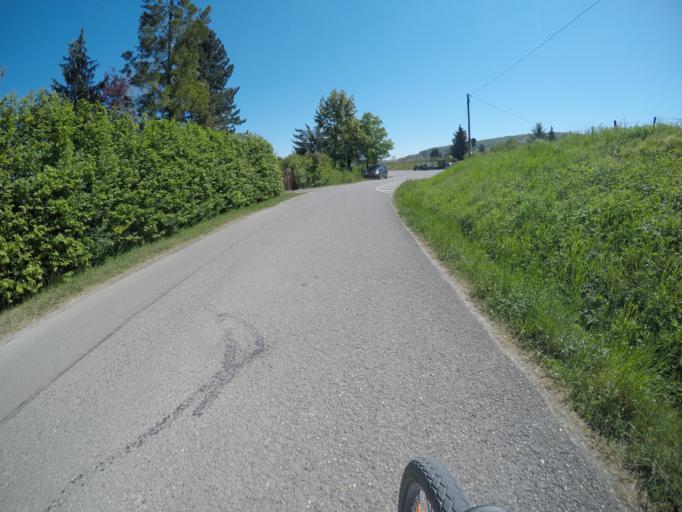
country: DE
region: Baden-Wuerttemberg
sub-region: Regierungsbezirk Stuttgart
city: Fellbach
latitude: 48.7989
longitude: 9.3011
